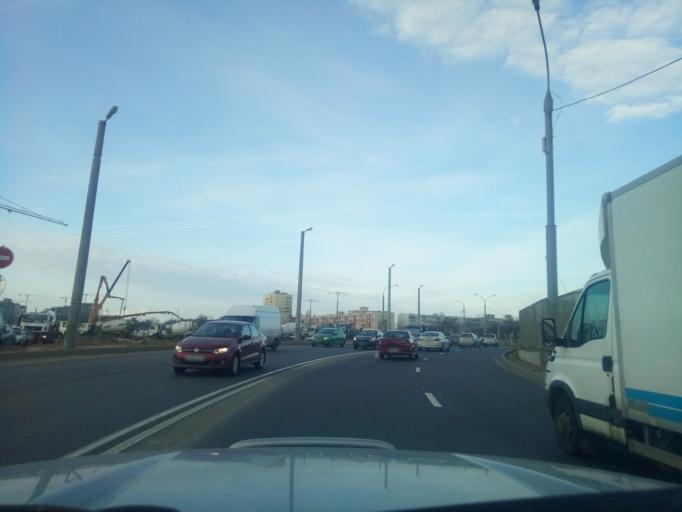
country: BY
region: Minsk
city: Minsk
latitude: 53.8720
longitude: 27.5464
